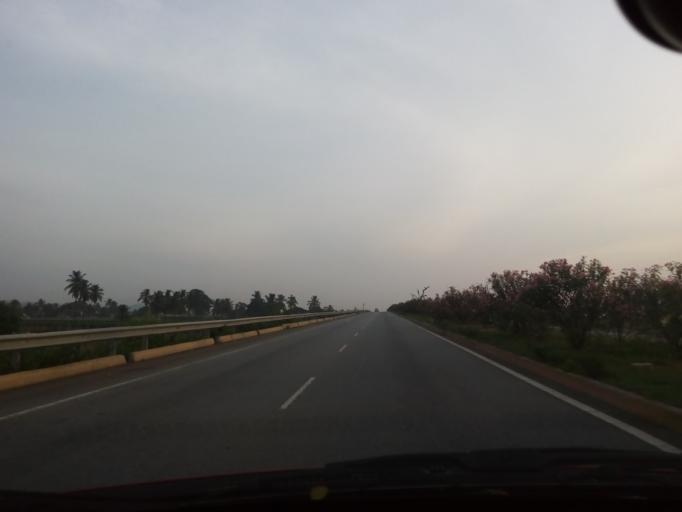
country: IN
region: Karnataka
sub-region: Chikkaballapur
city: Chik Ballapur
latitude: 13.3652
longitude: 77.7258
